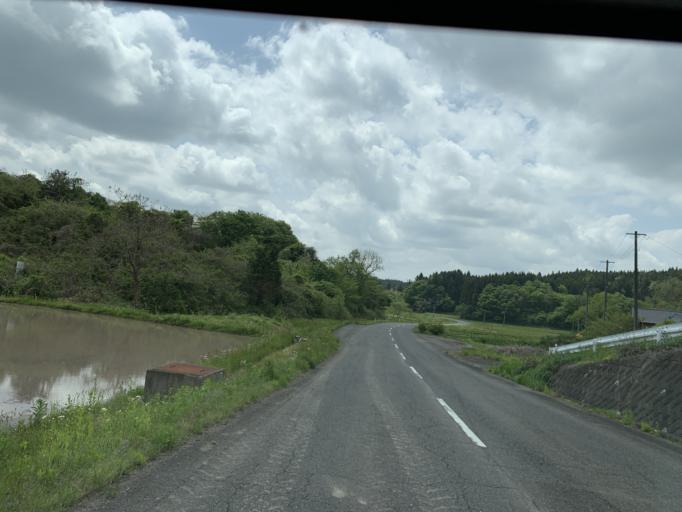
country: JP
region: Miyagi
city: Furukawa
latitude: 38.7090
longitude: 140.9181
